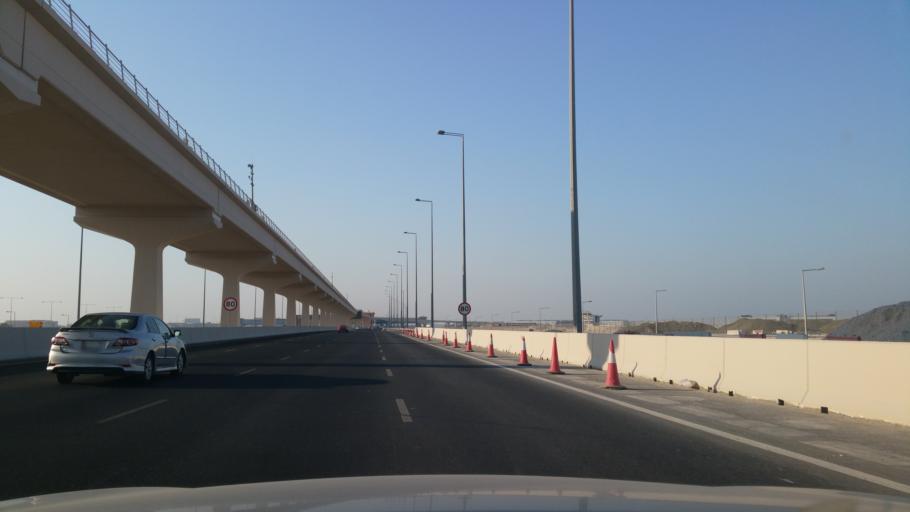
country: QA
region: Al Wakrah
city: Al Wakrah
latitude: 25.2020
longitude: 51.5918
